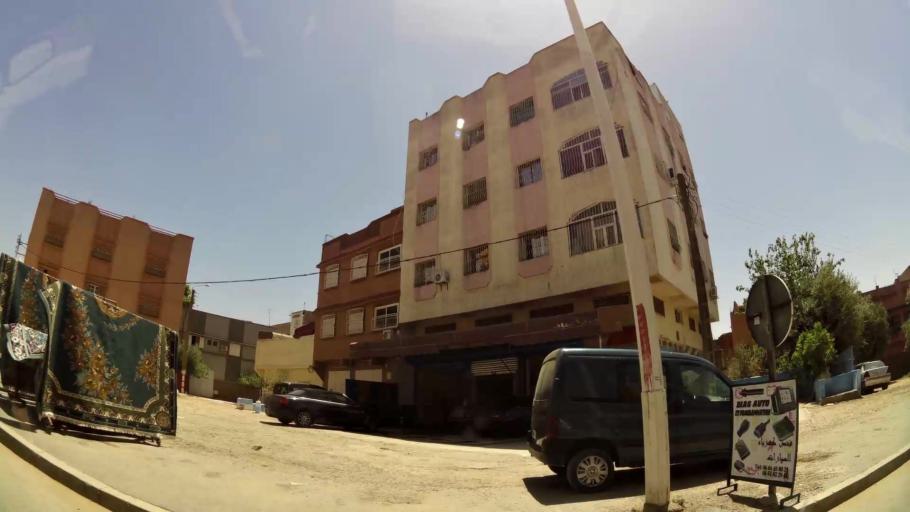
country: MA
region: Rabat-Sale-Zemmour-Zaer
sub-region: Khemisset
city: Khemisset
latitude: 33.8321
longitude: -6.0777
